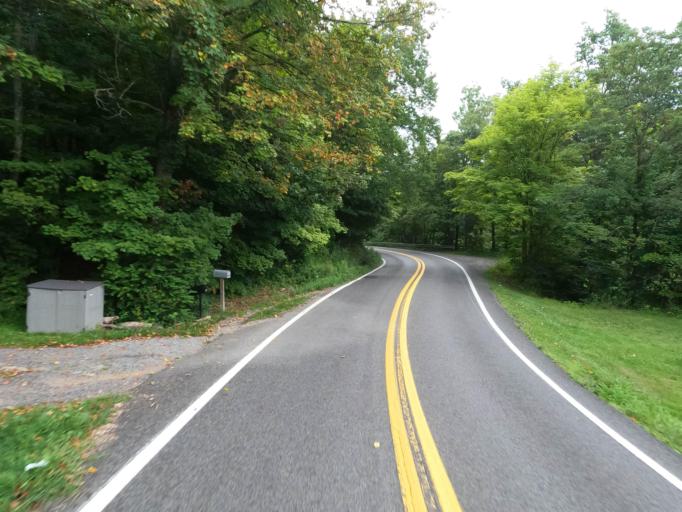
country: US
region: West Virginia
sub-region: Marion County
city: Fairmont
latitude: 39.5006
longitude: -80.1001
